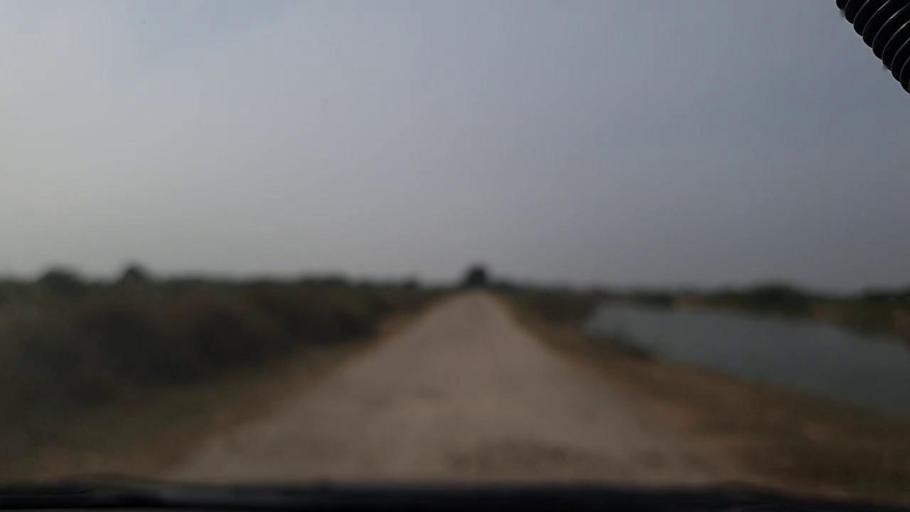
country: PK
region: Sindh
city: Thatta
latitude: 24.5700
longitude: 67.8720
